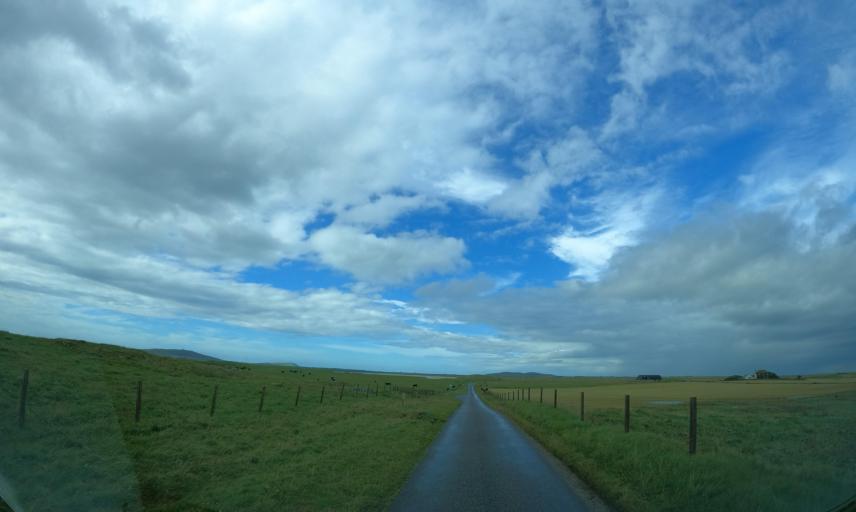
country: GB
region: Scotland
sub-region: Eilean Siar
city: Barra
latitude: 56.4923
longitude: -6.8398
